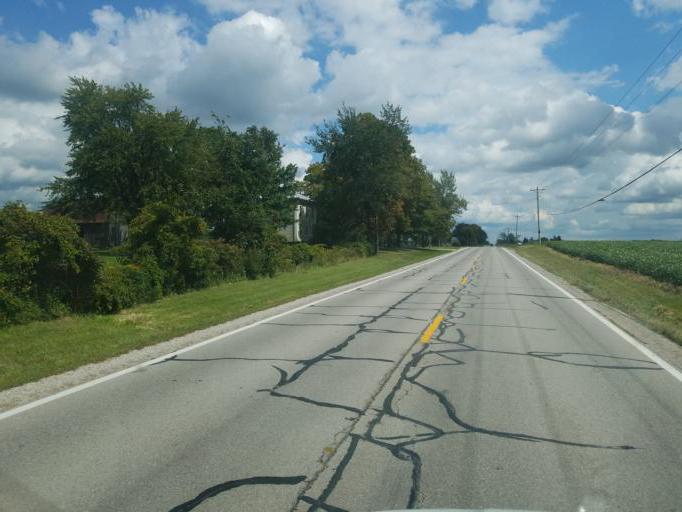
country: US
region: Ohio
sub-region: Huron County
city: Plymouth
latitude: 41.0310
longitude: -82.5995
